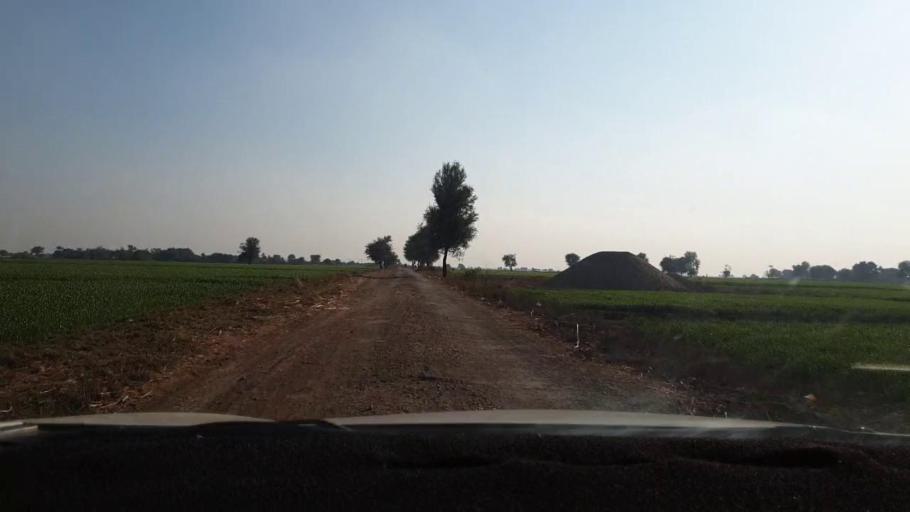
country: PK
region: Sindh
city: Berani
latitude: 25.7688
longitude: 68.7685
